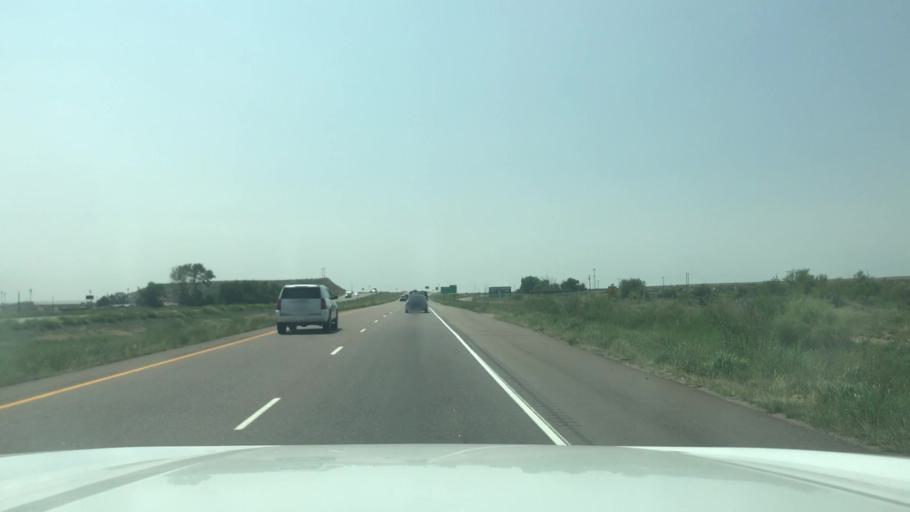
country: US
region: Colorado
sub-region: Pueblo County
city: Pueblo West
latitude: 38.4081
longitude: -104.6146
